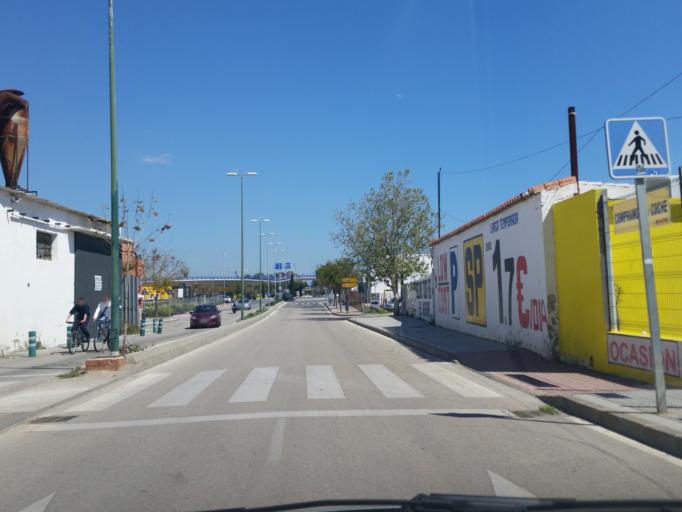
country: ES
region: Andalusia
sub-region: Provincia de Malaga
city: Torremolinos
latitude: 36.6679
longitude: -4.4732
